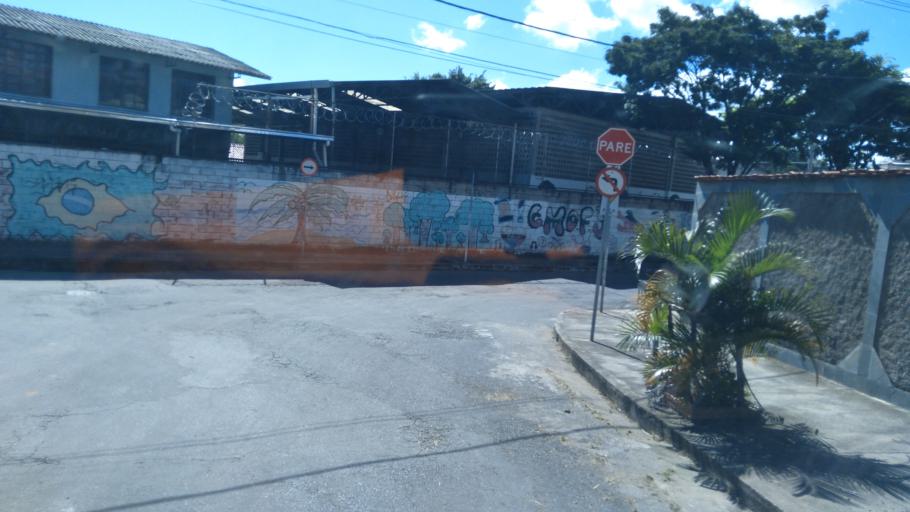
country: BR
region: Minas Gerais
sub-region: Belo Horizonte
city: Belo Horizonte
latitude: -19.8536
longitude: -43.9136
